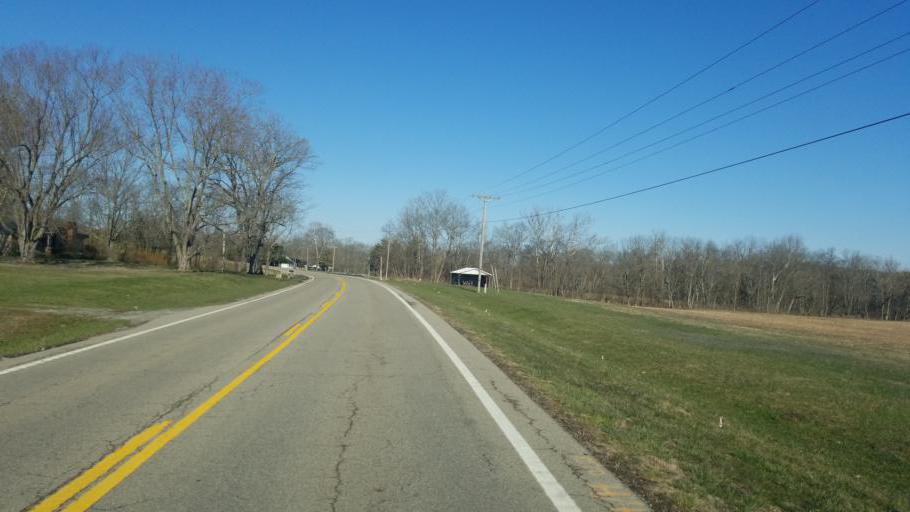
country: US
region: Ohio
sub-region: Highland County
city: Greenfield
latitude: 39.2293
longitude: -83.3224
